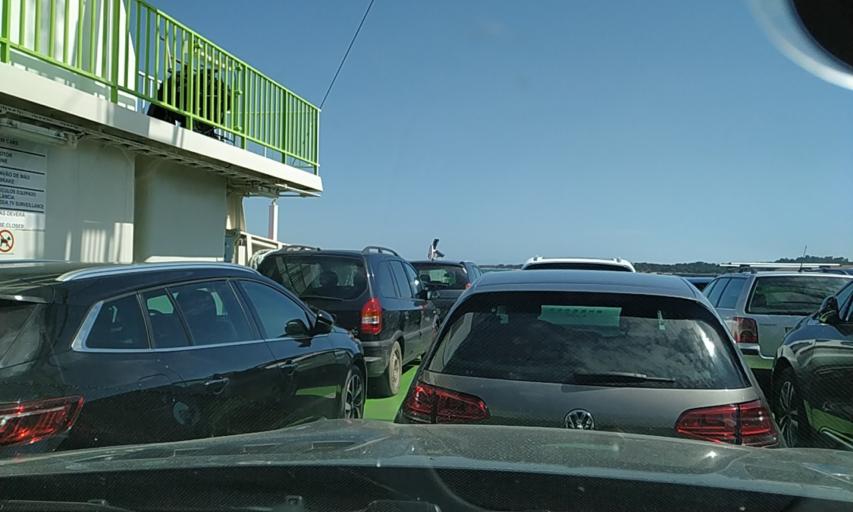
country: PT
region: Setubal
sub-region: Setubal
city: Setubal
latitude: 38.4803
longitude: -8.8723
